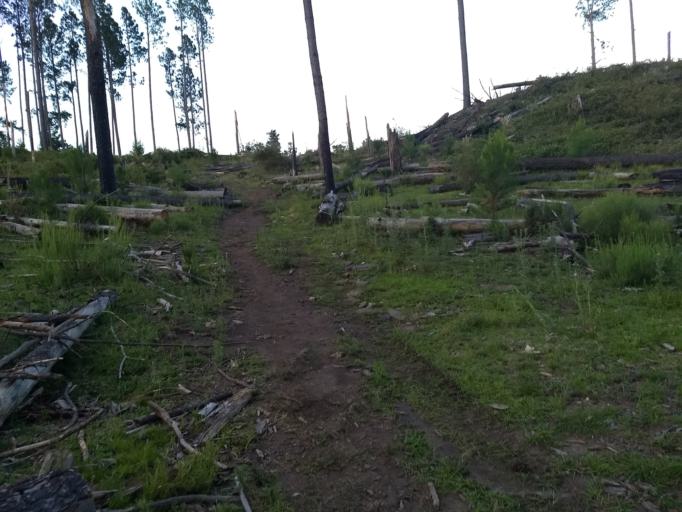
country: AR
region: Cordoba
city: Villa Berna
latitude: -31.9895
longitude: -64.8062
